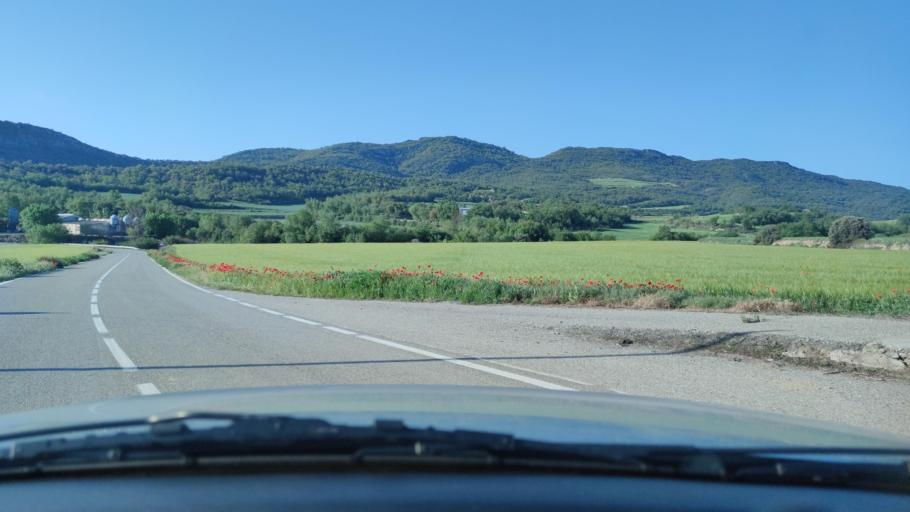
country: ES
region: Catalonia
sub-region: Provincia de Lleida
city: Cubells
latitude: 41.8891
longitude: 0.9880
